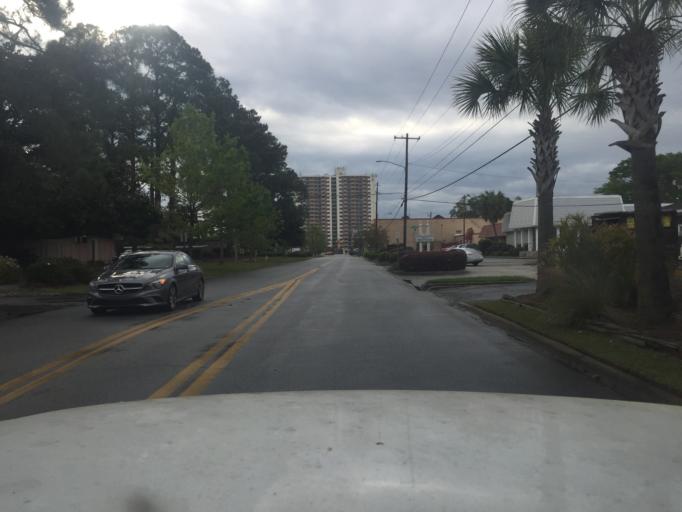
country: US
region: Georgia
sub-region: Chatham County
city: Thunderbolt
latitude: 32.0305
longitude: -81.0953
